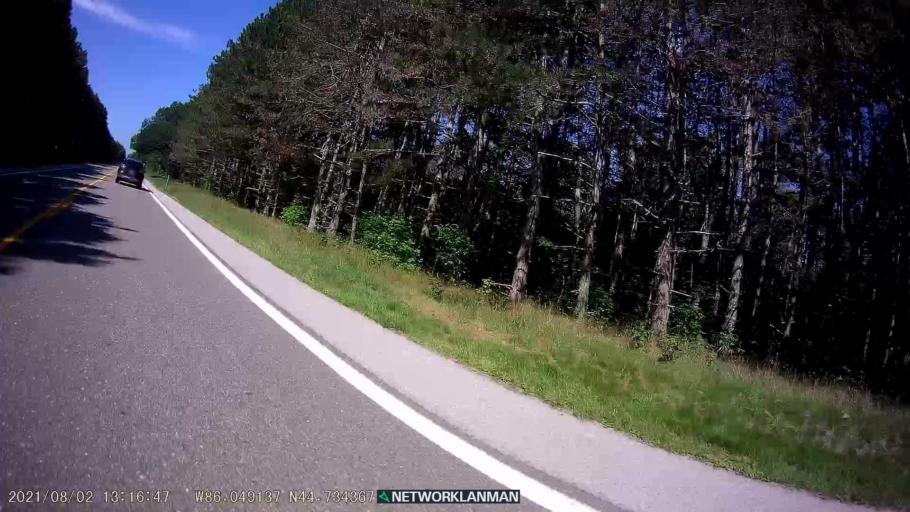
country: US
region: Michigan
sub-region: Benzie County
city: Beulah
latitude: 44.7345
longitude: -86.0493
